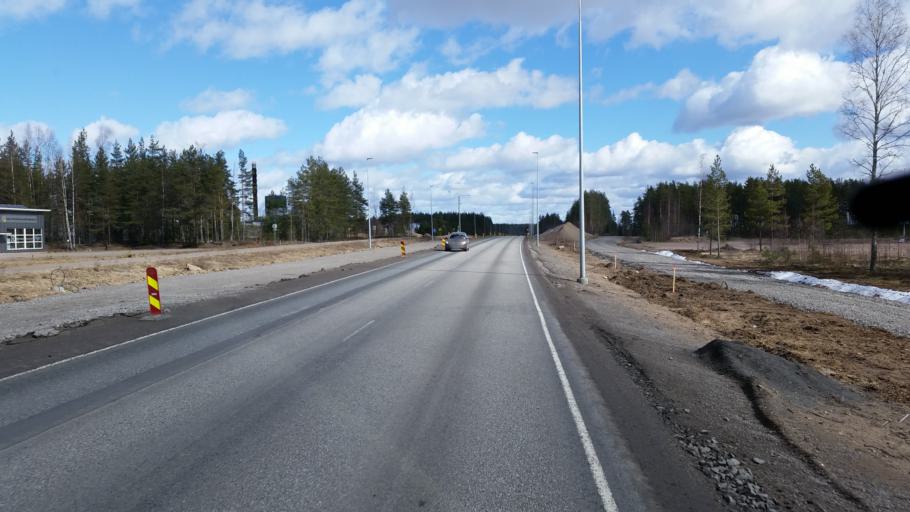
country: FI
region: South Karelia
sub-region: Lappeenranta
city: Luumaeki
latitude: 60.9321
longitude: 27.6511
